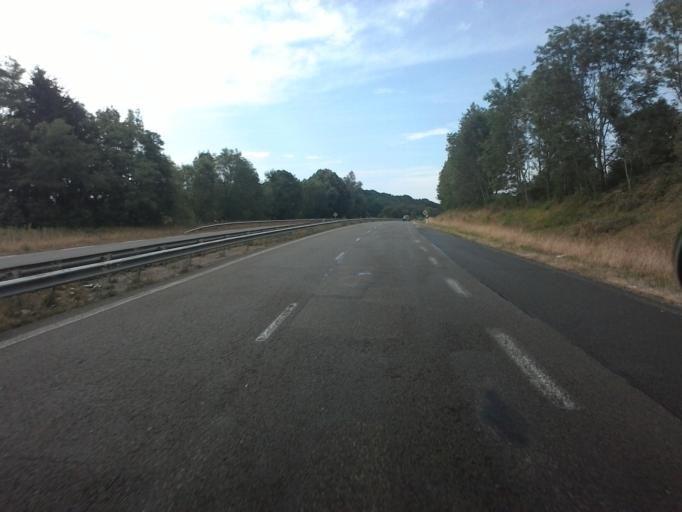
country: FR
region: Franche-Comte
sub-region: Departement du Jura
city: Lons-le-Saunier
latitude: 46.7223
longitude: 5.5575
